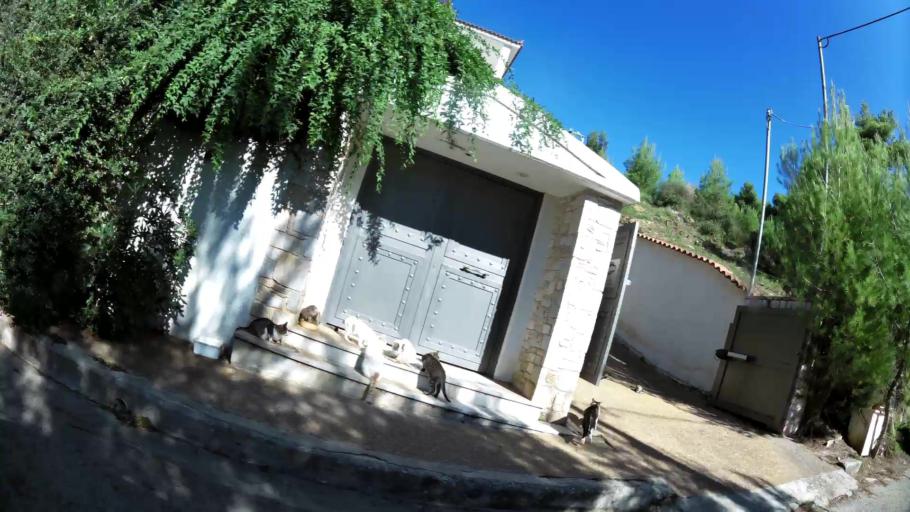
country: GR
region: Attica
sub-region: Nomarchia Anatolikis Attikis
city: Rodopoli
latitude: 38.1100
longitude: 23.8809
